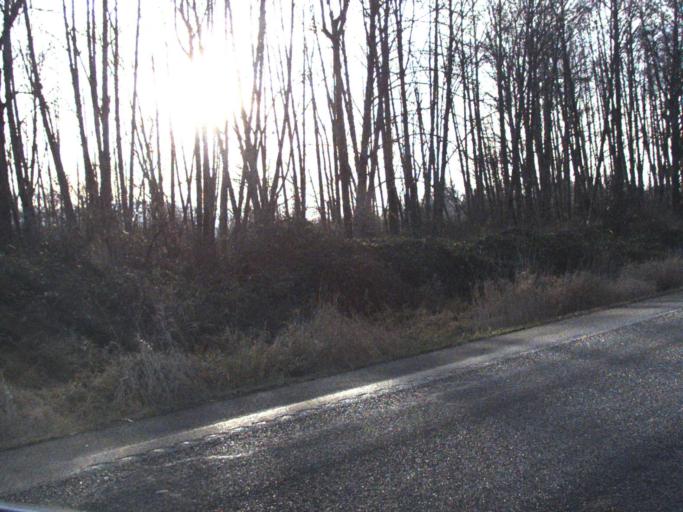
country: US
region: Washington
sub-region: Skagit County
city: Sedro-Woolley
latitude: 48.5280
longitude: -122.1707
